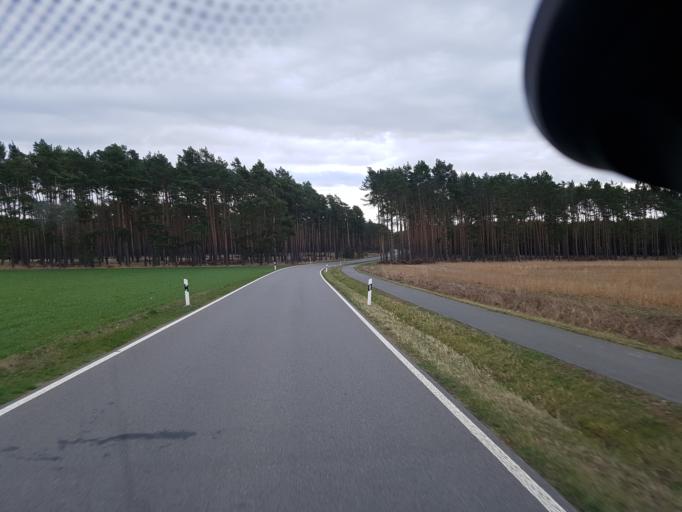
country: DE
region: Brandenburg
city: Mixdorf
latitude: 52.2018
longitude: 14.3726
